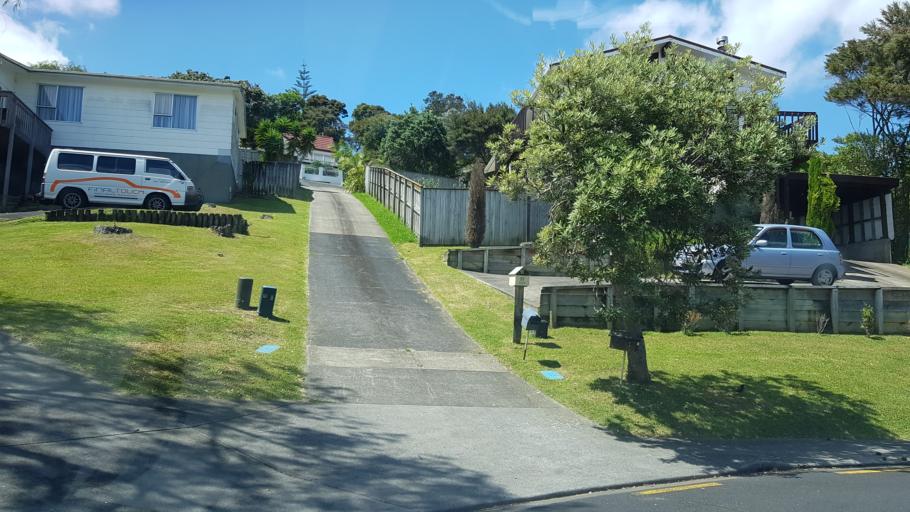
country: NZ
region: Auckland
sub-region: Auckland
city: North Shore
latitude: -36.7882
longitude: 174.7152
